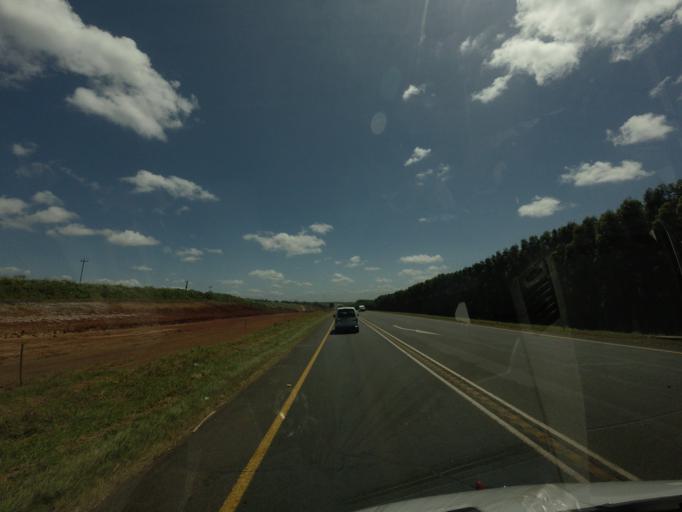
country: ZA
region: KwaZulu-Natal
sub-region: uThungulu District Municipality
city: Empangeni
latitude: -28.7975
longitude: 31.9210
